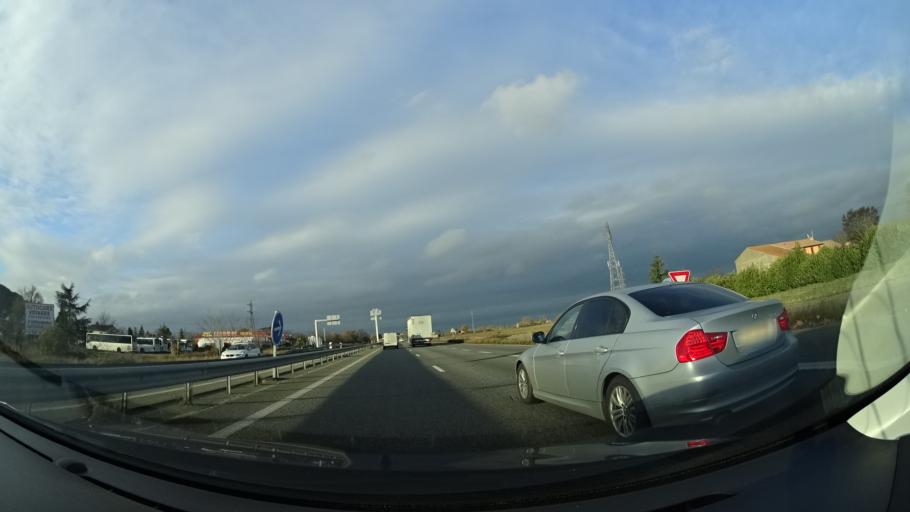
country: FR
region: Midi-Pyrenees
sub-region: Departement de l'Ariege
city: La Tour-du-Crieu
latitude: 43.1167
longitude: 1.6304
